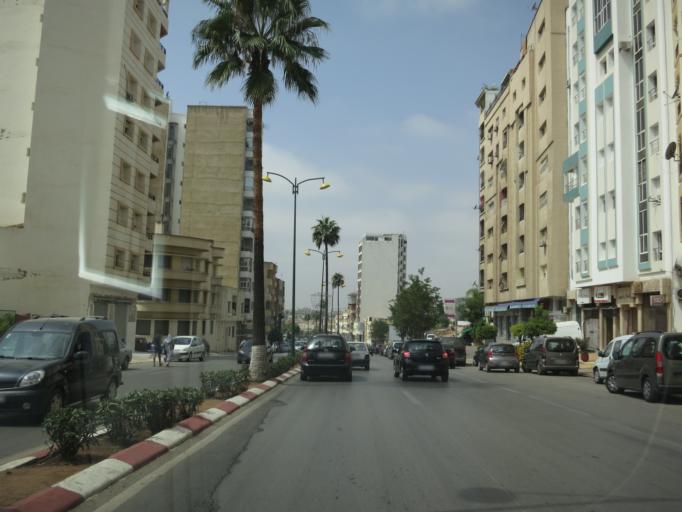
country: MA
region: Meknes-Tafilalet
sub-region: Meknes
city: Meknes
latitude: 33.8959
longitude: -5.5465
